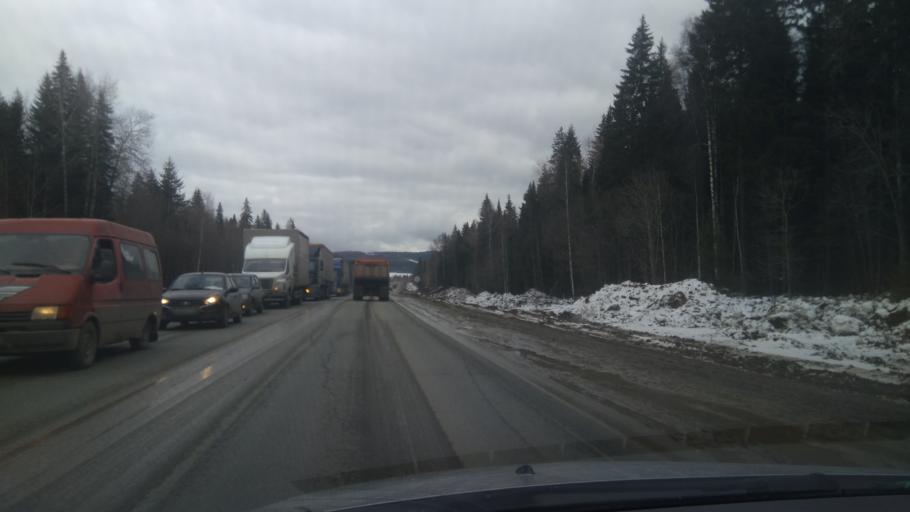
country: RU
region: Sverdlovsk
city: Bisert'
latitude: 56.8294
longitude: 59.1332
